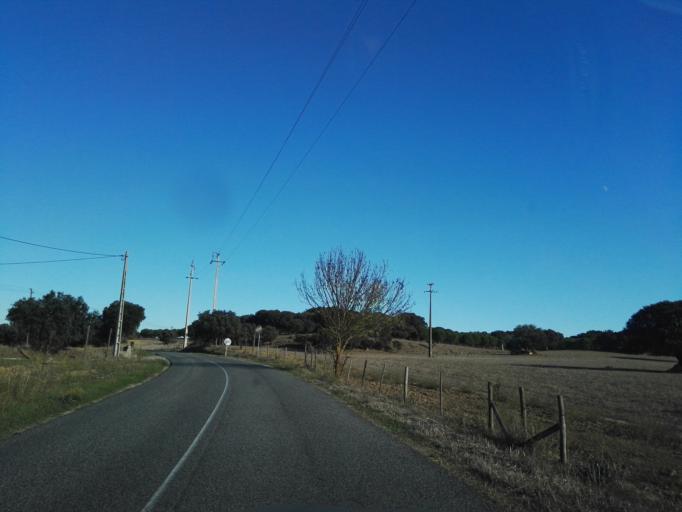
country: PT
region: Evora
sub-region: Arraiolos
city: Arraiolos
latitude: 38.6467
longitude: -7.9610
